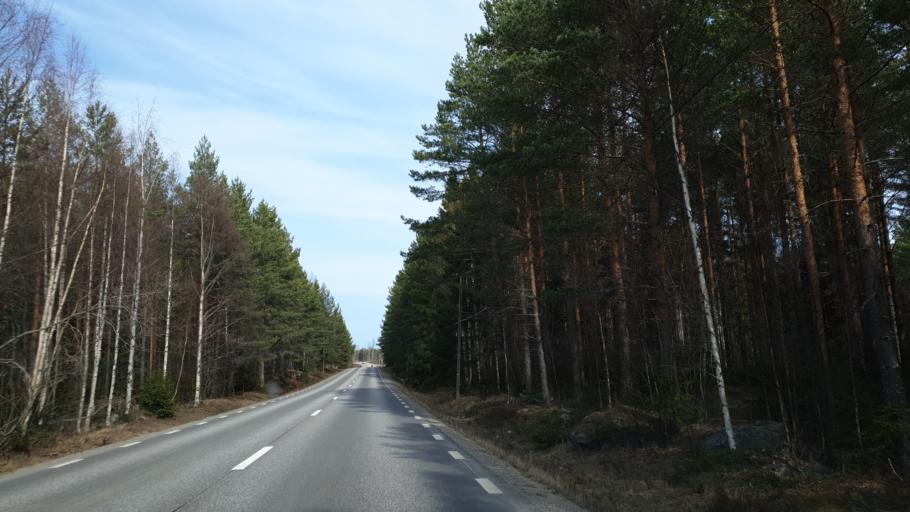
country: SE
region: Gaevleborg
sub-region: Gavle Kommun
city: Norrsundet
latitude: 61.0124
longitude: 17.1381
